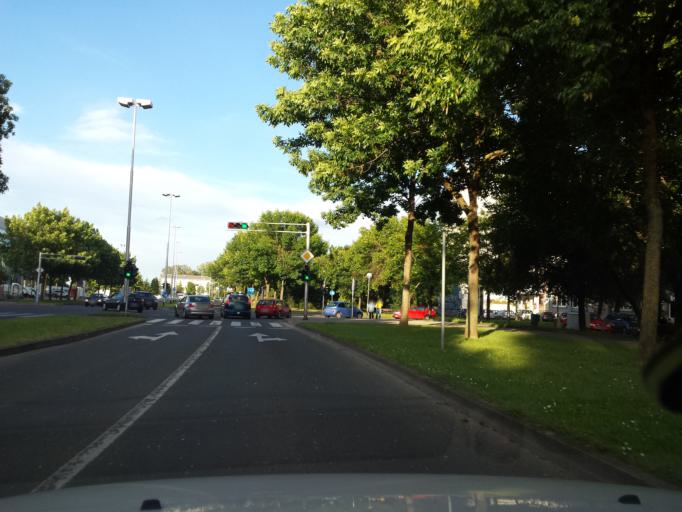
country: HR
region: Grad Zagreb
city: Novi Zagreb
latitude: 45.7729
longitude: 16.0012
